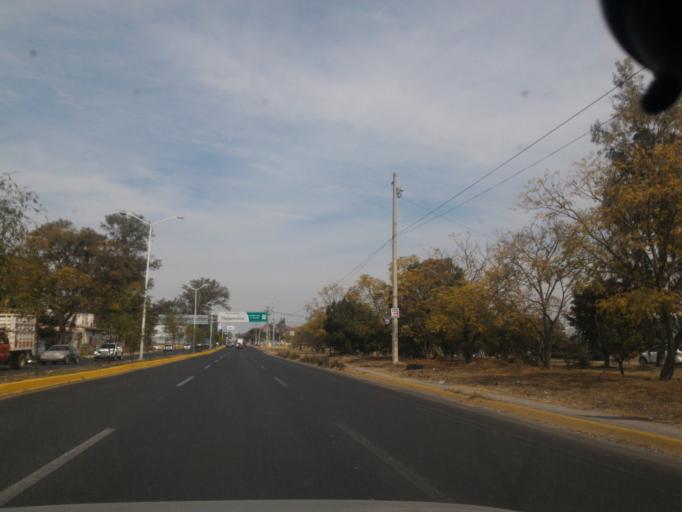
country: MX
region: Jalisco
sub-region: Tlajomulco de Zuniga
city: La Tijera
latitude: 20.5783
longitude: -103.4311
